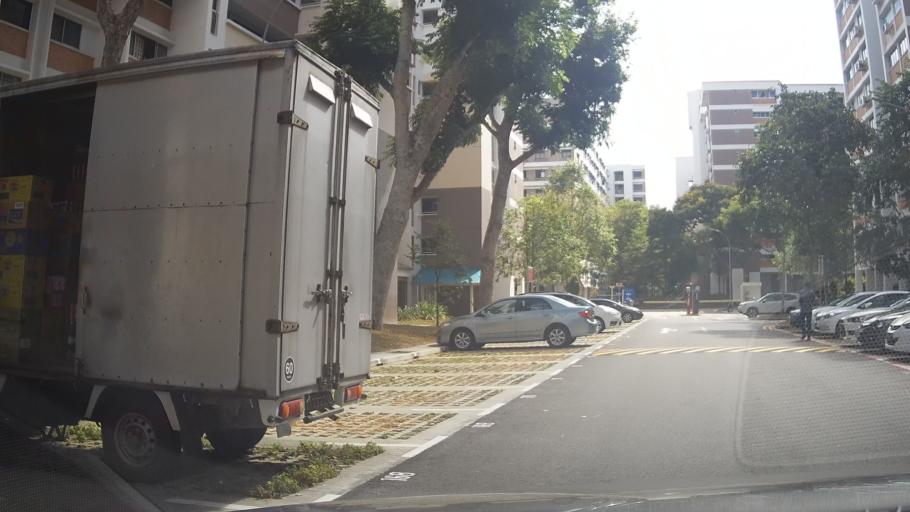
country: SG
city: Singapore
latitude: 1.3492
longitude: 103.9528
